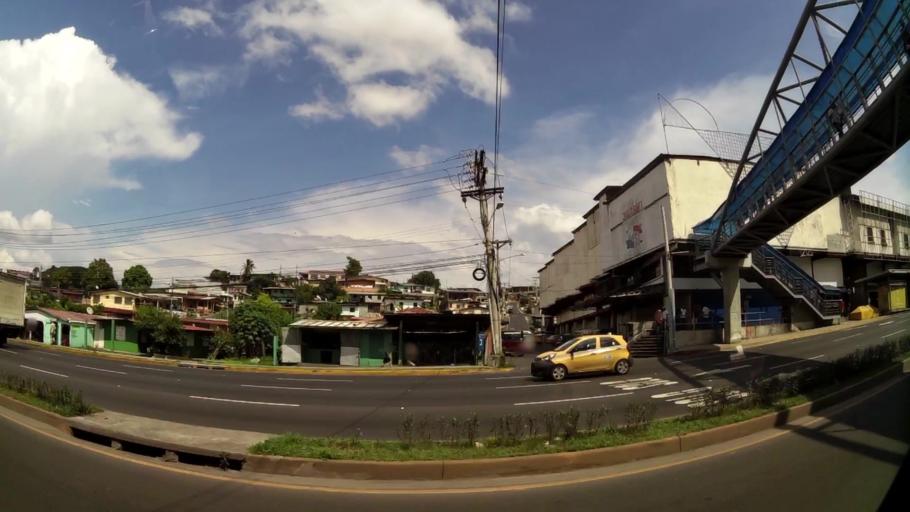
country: PA
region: Panama
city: San Miguelito
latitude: 9.0307
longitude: -79.5024
